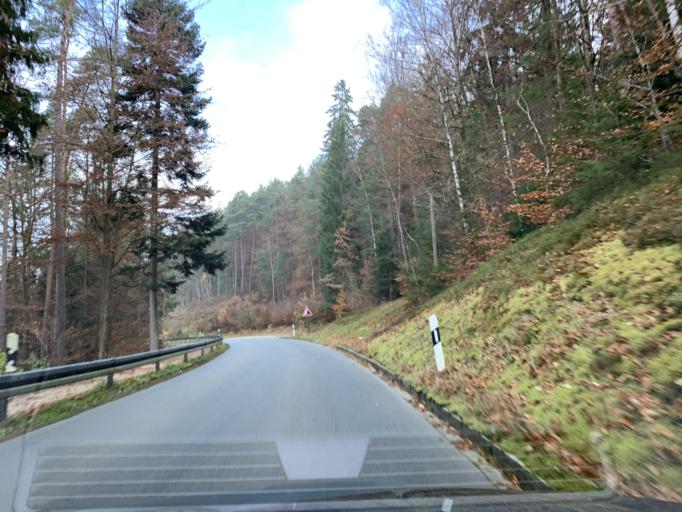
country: DE
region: Bavaria
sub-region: Upper Palatinate
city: Thanstein
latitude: 49.3526
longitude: 12.4493
